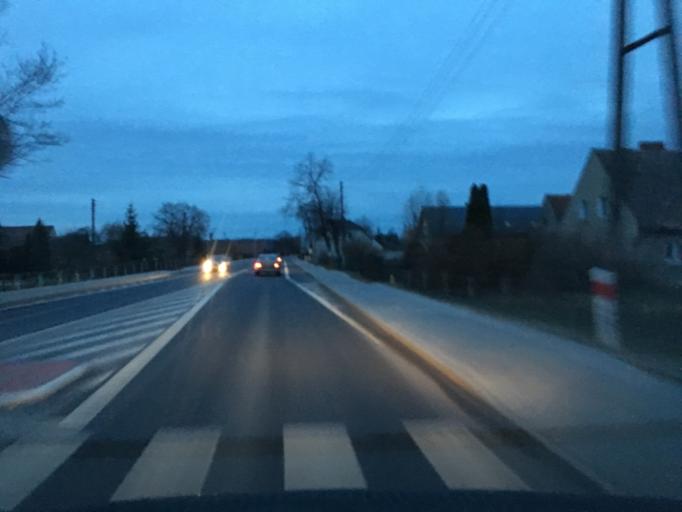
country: PL
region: Opole Voivodeship
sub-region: Powiat opolski
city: Dabrowa
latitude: 50.7225
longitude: 17.7590
